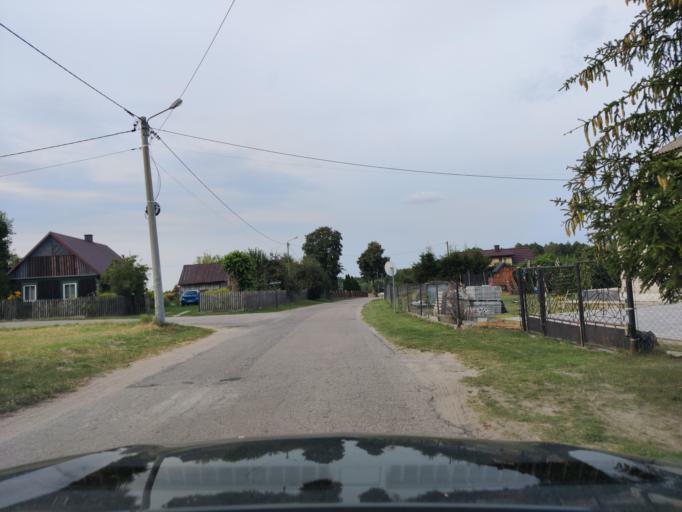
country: PL
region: Masovian Voivodeship
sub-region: Powiat pultuski
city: Obryte
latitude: 52.7407
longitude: 21.2521
